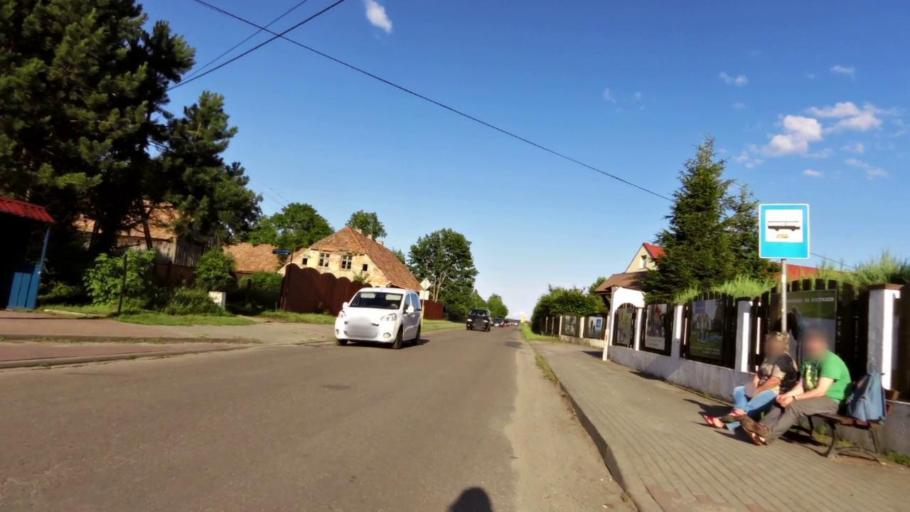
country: PL
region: West Pomeranian Voivodeship
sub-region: Powiat slawienski
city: Darlowo
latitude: 54.3947
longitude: 16.3481
